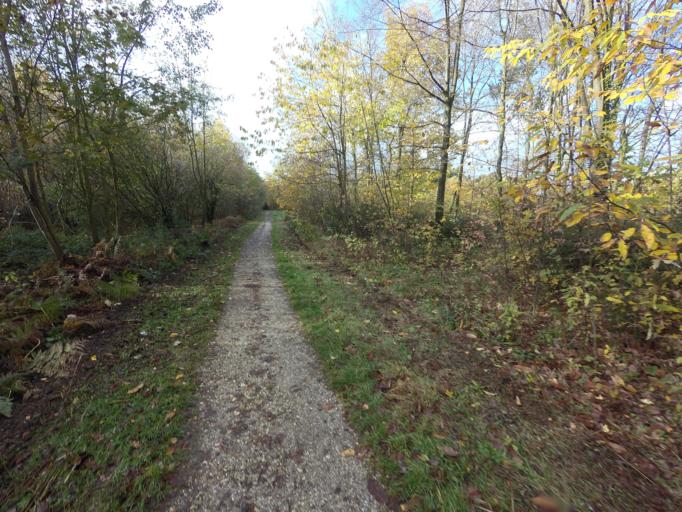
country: NL
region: Limburg
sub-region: Gemeente Vaals
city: Vaals
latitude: 50.7561
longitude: 6.0164
